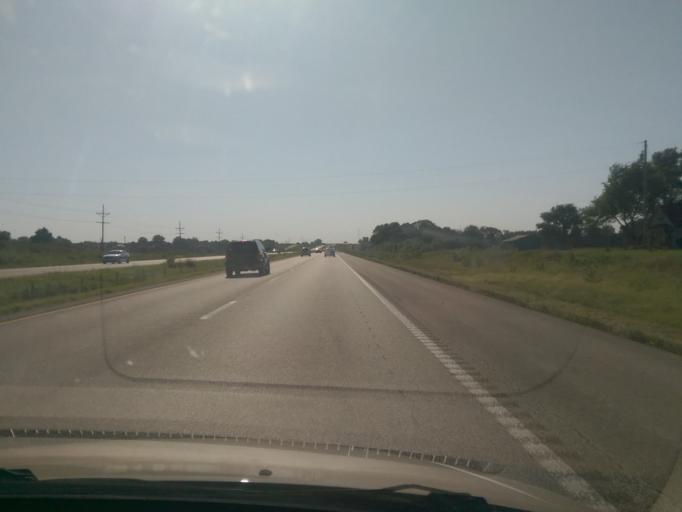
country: US
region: Missouri
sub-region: Saline County
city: Sweet Springs
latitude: 38.9782
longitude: -93.4448
